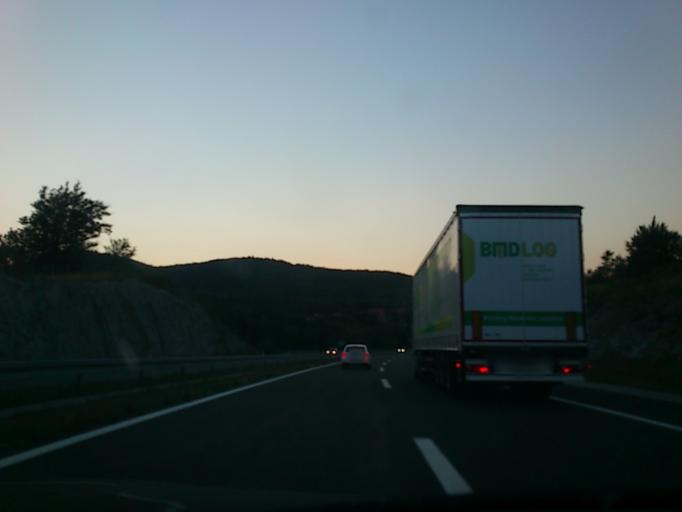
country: HR
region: Karlovacka
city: Ostarije
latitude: 45.1222
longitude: 15.2441
